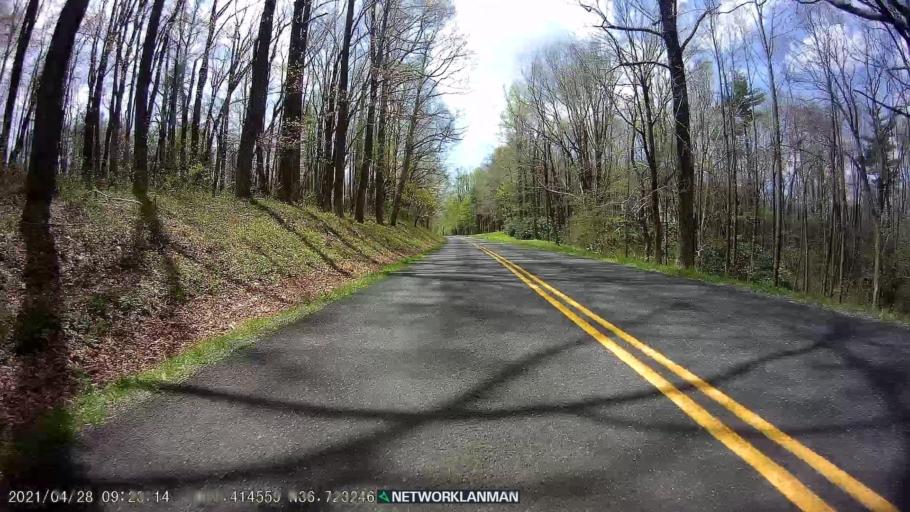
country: US
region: Virginia
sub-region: Patrick County
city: Stuart
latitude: 36.7233
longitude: -80.4145
